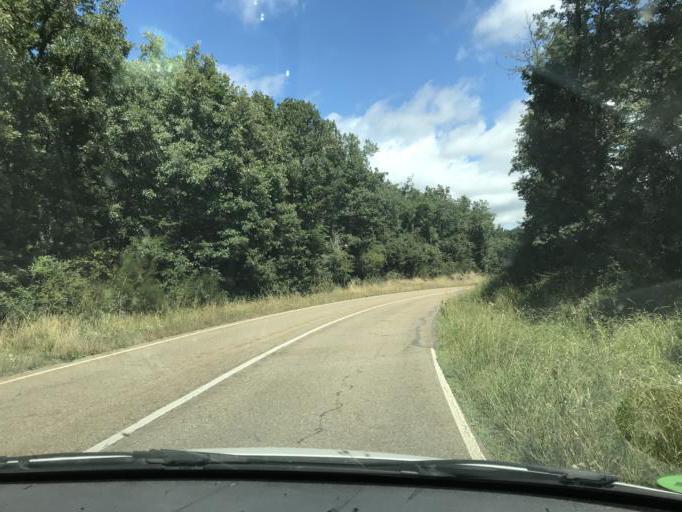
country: ES
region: Castille and Leon
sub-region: Provincia de Palencia
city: Cervera de Pisuerga
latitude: 42.9071
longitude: -4.4934
